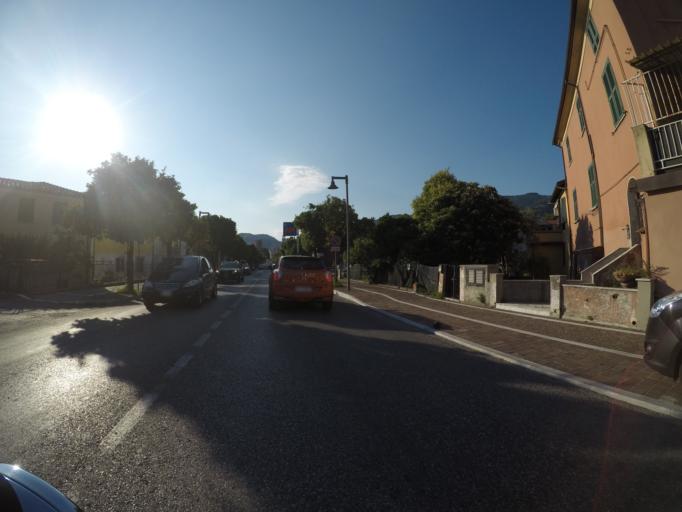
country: IT
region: Tuscany
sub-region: Provincia di Massa-Carrara
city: Massa
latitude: 44.0319
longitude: 10.1436
